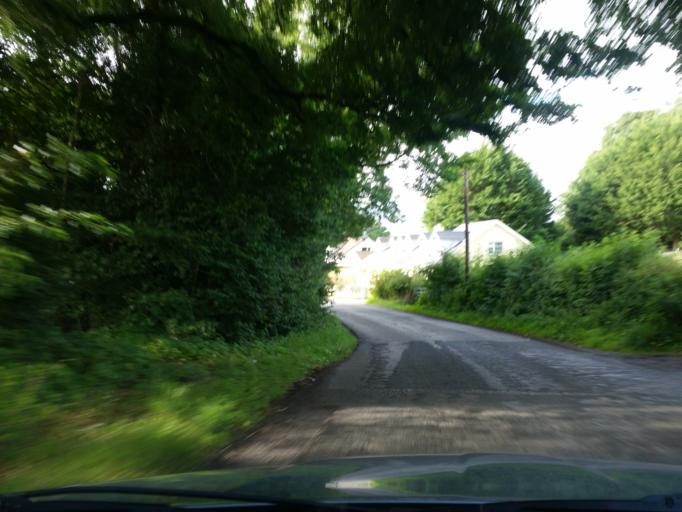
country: IE
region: Ulster
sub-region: County Monaghan
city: Clones
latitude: 54.1939
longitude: -7.2499
